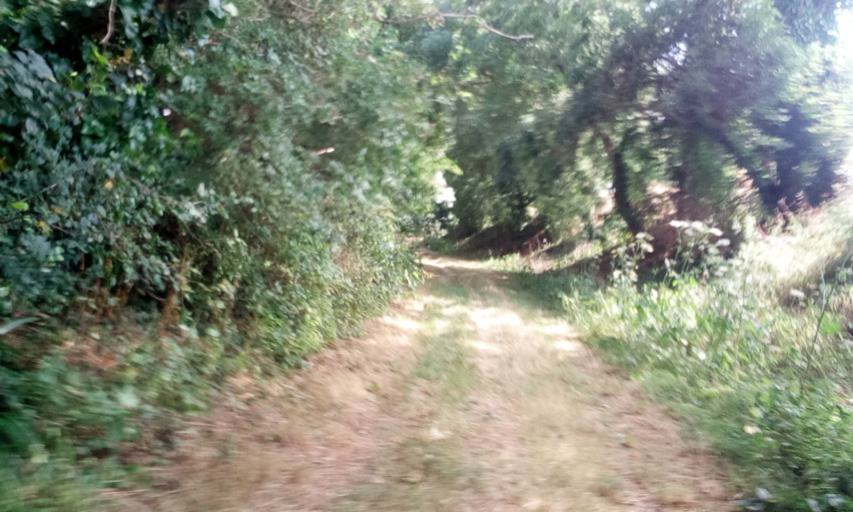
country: FR
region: Lower Normandy
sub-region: Departement du Calvados
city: Douvres-la-Delivrande
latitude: 49.2954
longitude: -0.4025
